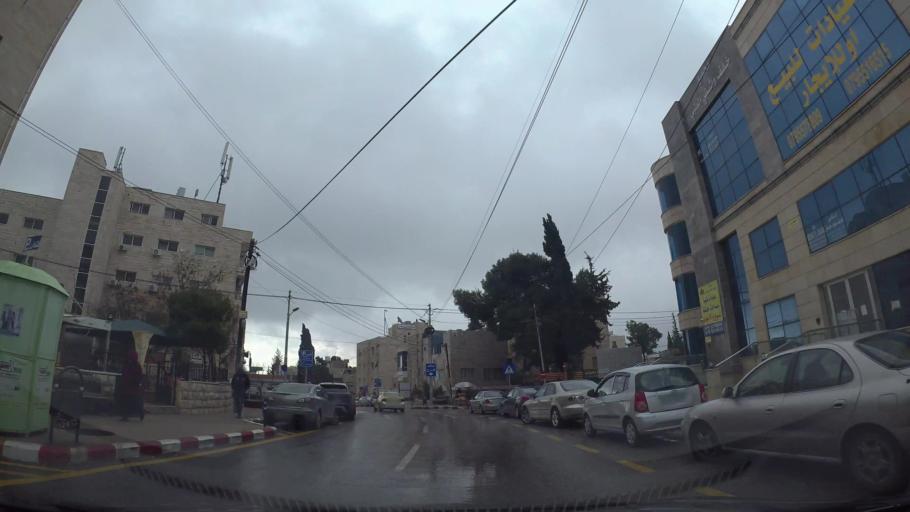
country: JO
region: Amman
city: Amman
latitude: 31.9502
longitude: 35.9047
